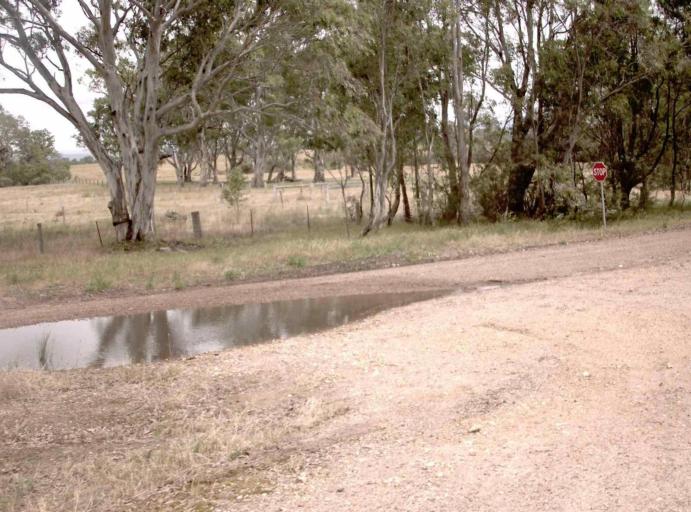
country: AU
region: Victoria
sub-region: Wellington
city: Sale
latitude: -37.8860
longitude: 147.0644
